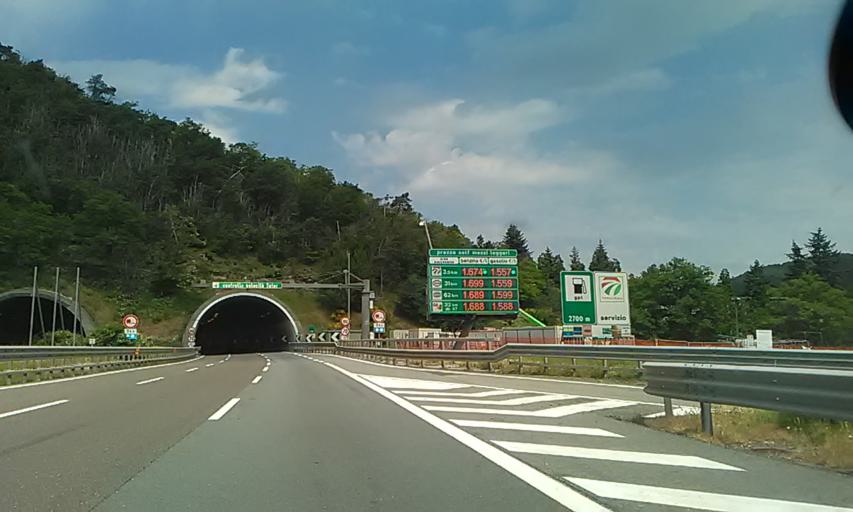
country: IT
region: Liguria
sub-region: Provincia di Genova
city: Rossiglione
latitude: 44.5598
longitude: 8.6677
